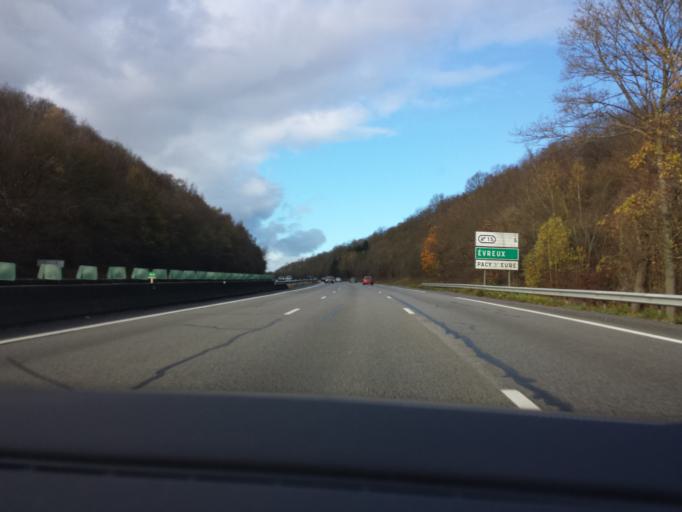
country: FR
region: Ile-de-France
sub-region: Departement des Yvelines
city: Bonnieres-sur-Seine
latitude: 49.0178
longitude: 1.5837
